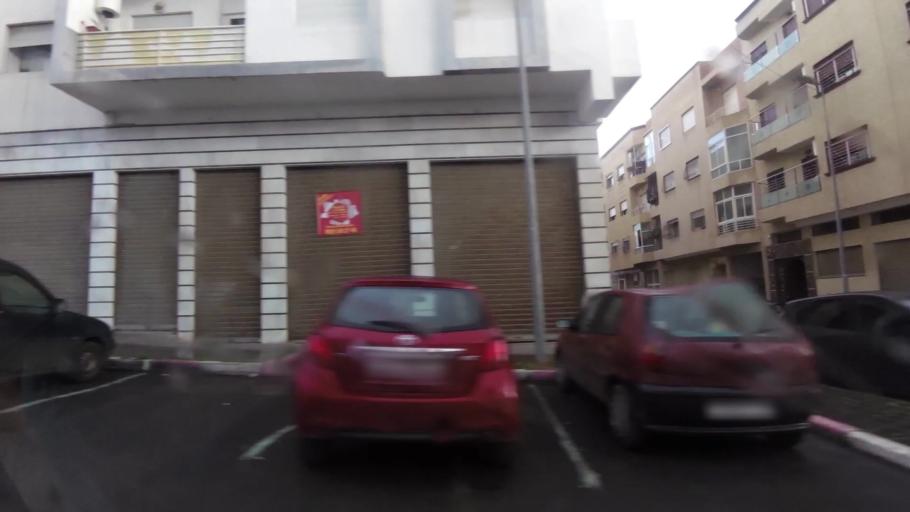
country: MA
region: Grand Casablanca
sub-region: Casablanca
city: Casablanca
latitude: 33.5373
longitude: -7.6715
